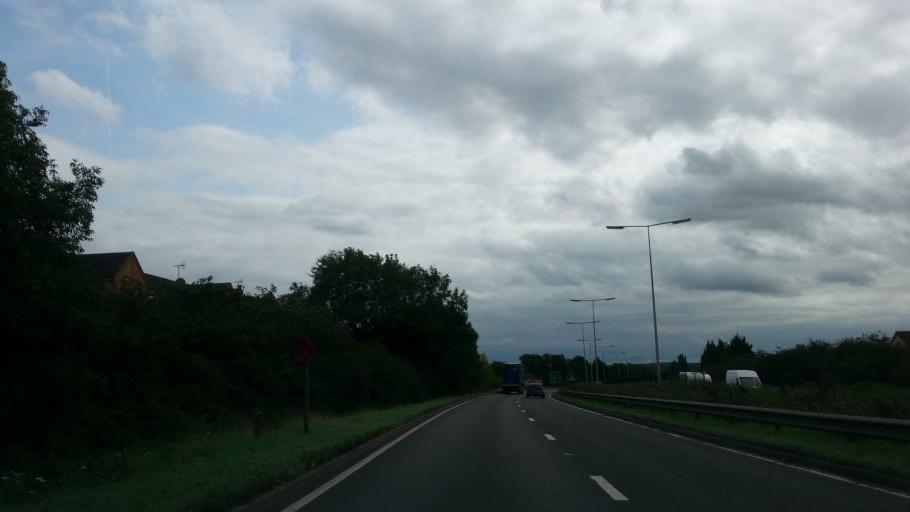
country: GB
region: England
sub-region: Northamptonshire
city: Hardingstone
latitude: 52.2084
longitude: -0.8925
